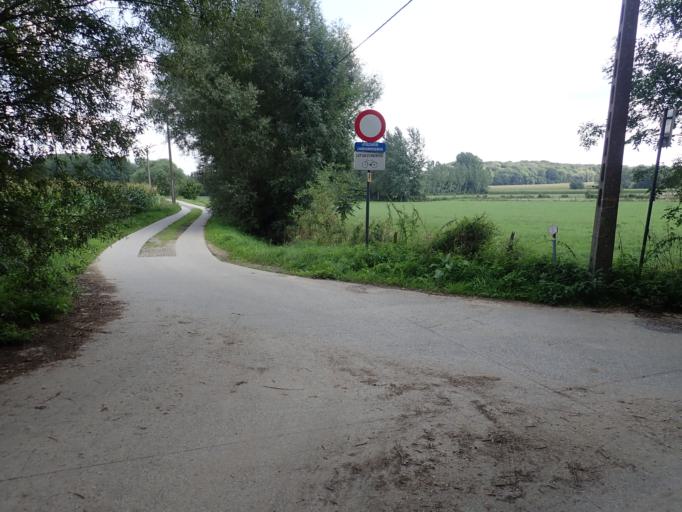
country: BE
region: Flanders
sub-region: Provincie Vlaams-Brabant
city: Asse
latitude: 50.9354
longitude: 4.1854
